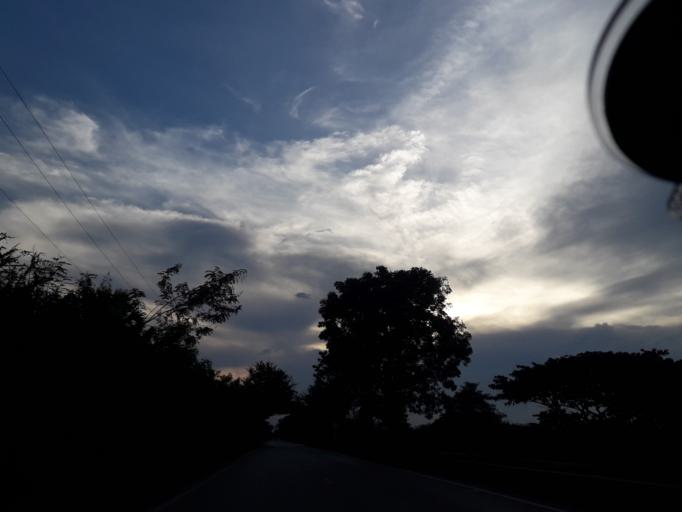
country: TH
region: Sara Buri
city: Nong Khae
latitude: 14.2727
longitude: 100.8848
